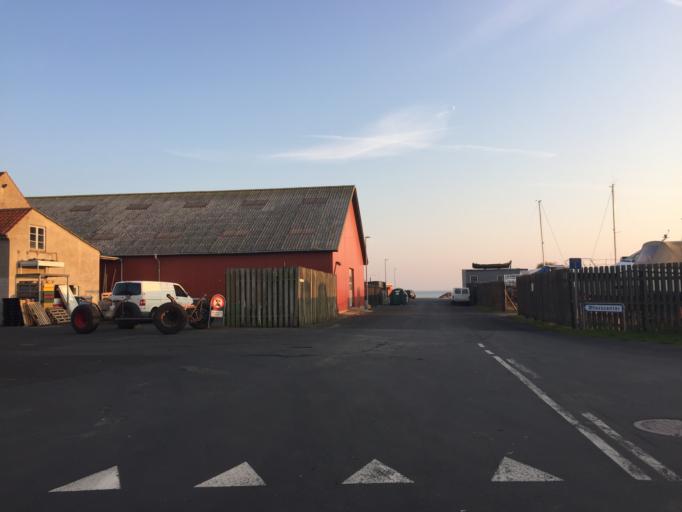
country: DK
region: South Denmark
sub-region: Faaborg-Midtfyn Kommune
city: Faaborg
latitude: 55.0950
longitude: 10.2369
